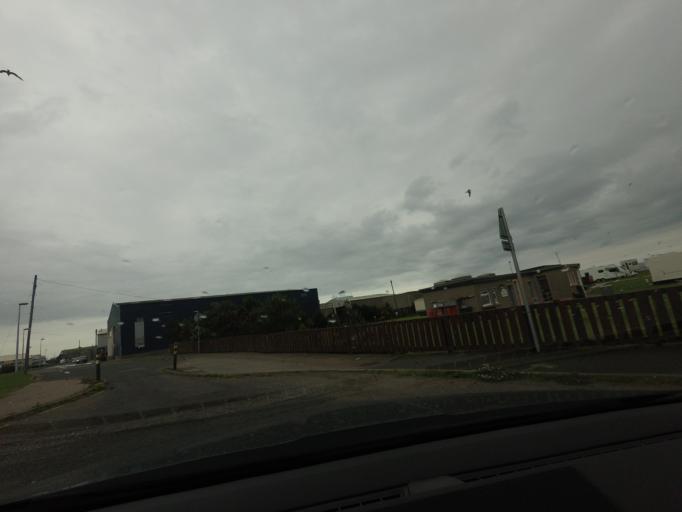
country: GB
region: Scotland
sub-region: Aberdeenshire
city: Fraserburgh
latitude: 57.6868
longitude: -2.0014
